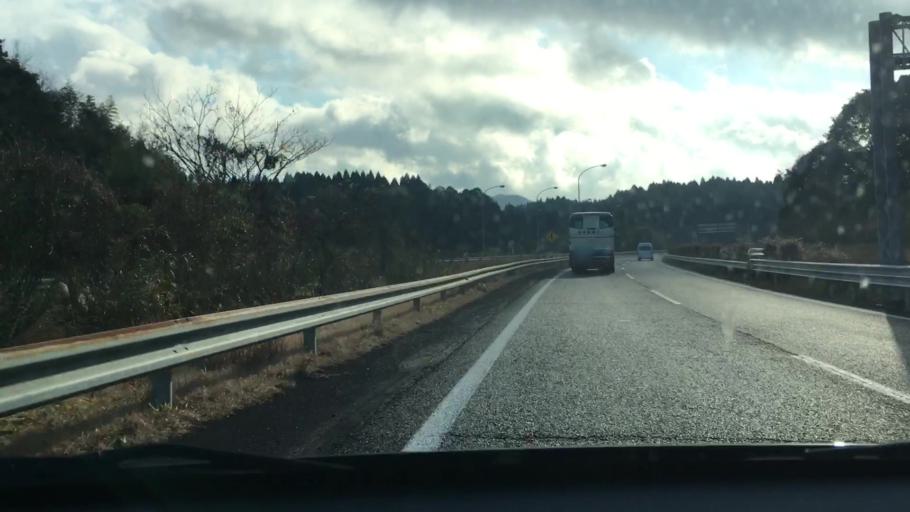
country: JP
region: Kagoshima
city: Okuchi-shinohara
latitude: 32.0294
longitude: 130.7972
